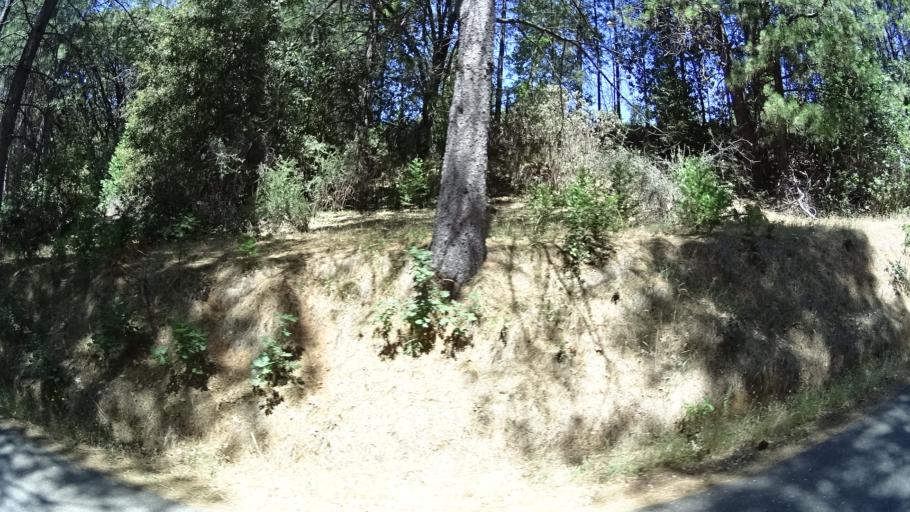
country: US
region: California
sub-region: Amador County
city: Pioneer
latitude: 38.4159
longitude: -120.5218
